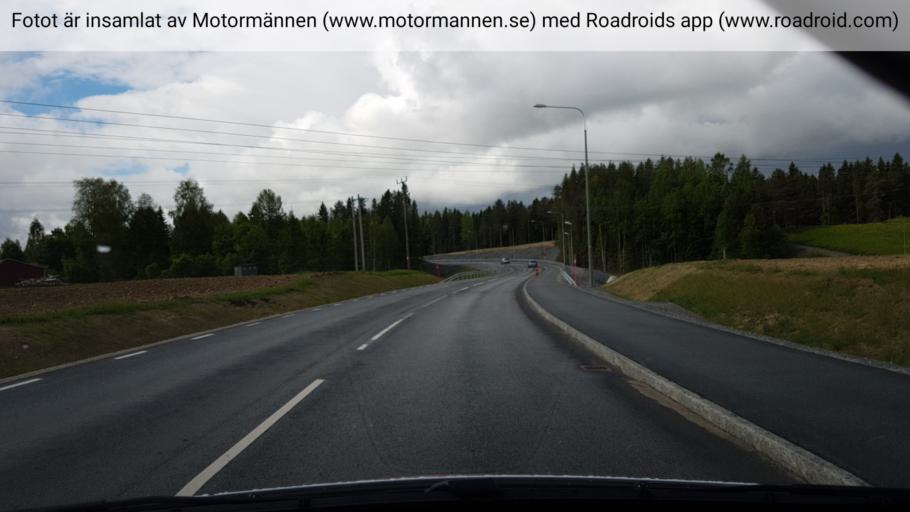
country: SE
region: Vaesterbotten
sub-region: Vannas Kommun
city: Vaennaes
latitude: 63.9142
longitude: 19.7734
